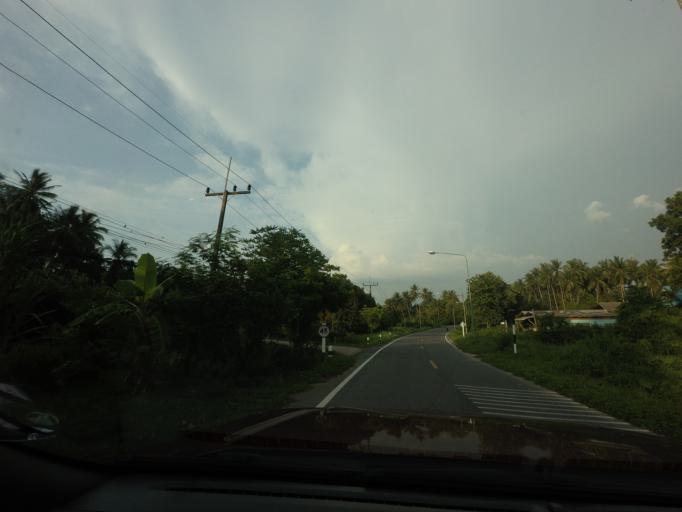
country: TH
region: Pattani
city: Khok Pho
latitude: 6.6701
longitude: 101.1021
